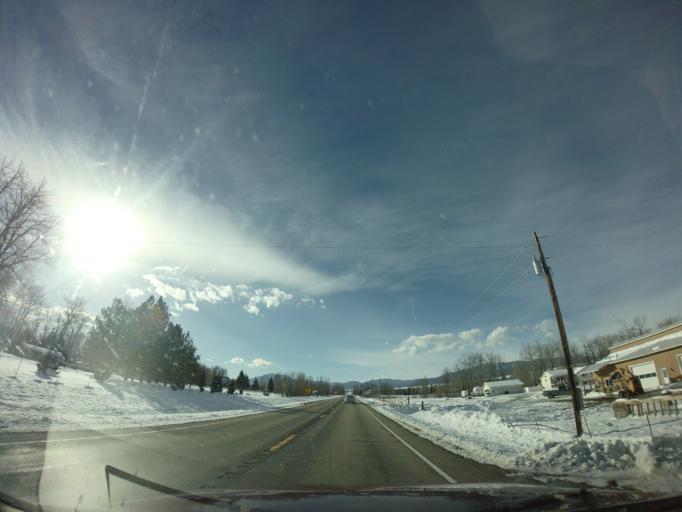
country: US
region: Montana
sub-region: Carbon County
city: Red Lodge
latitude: 45.2578
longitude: -109.2289
